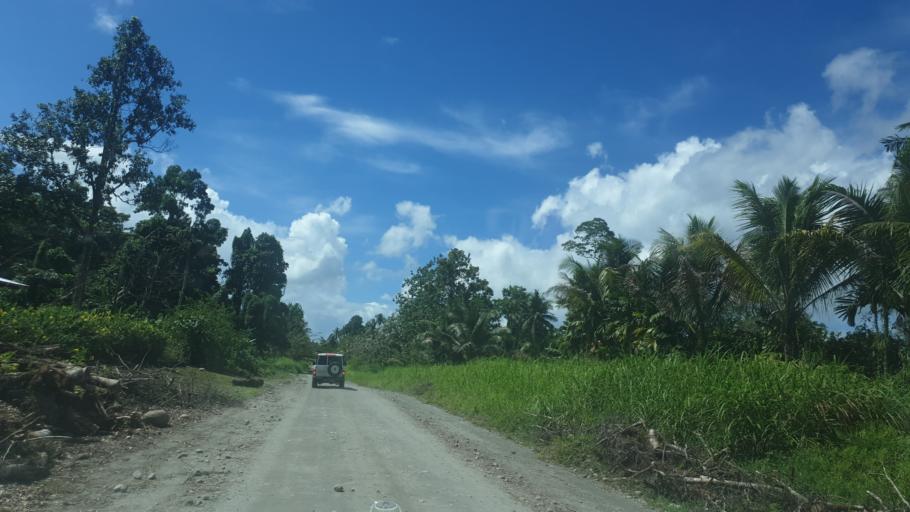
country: PG
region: Bougainville
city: Panguna
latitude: -6.6617
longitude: 155.4546
